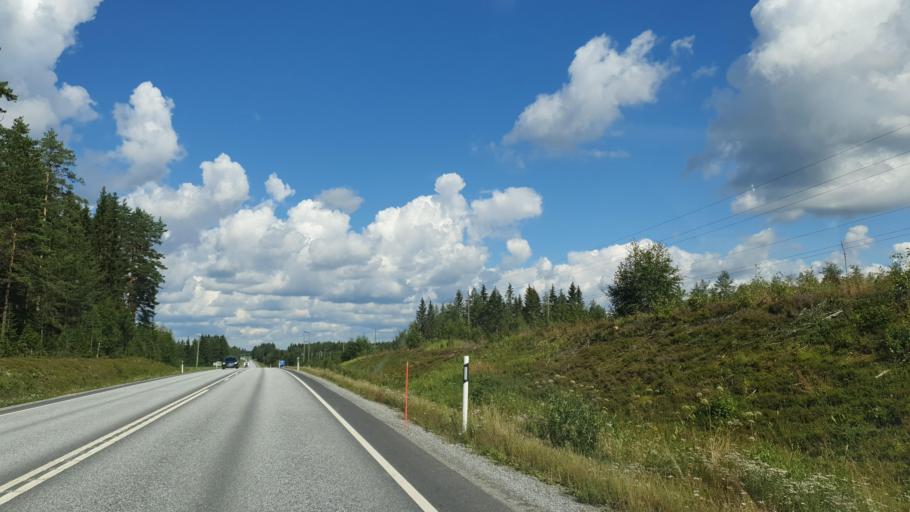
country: FI
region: Northern Savo
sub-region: Ylae-Savo
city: Sonkajaervi
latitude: 63.8511
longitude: 27.4405
